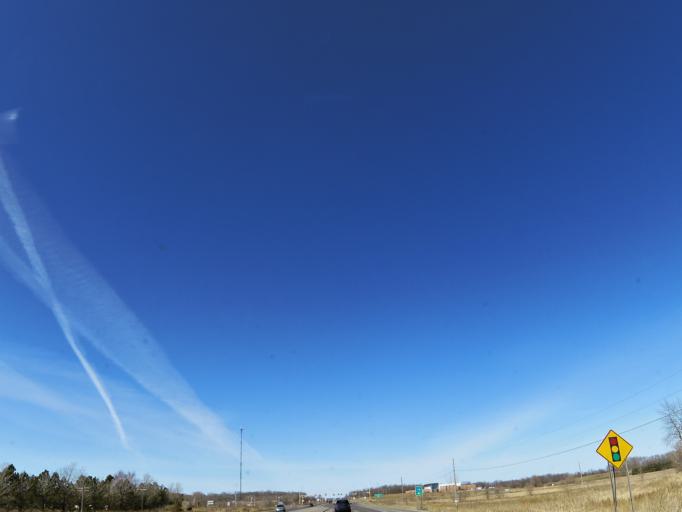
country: US
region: Minnesota
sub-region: Hennepin County
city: Medina
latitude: 45.0504
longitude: -93.5589
